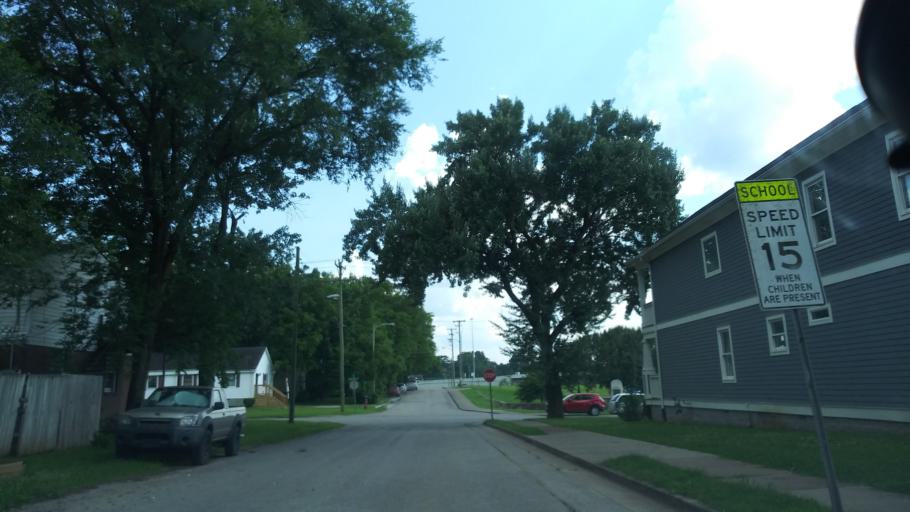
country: US
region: Tennessee
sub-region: Davidson County
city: Nashville
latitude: 36.1571
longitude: -86.8438
